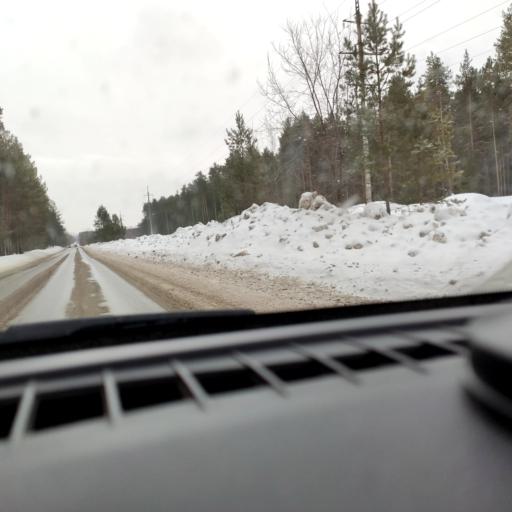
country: RU
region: Perm
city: Perm
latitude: 58.0590
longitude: 56.2694
